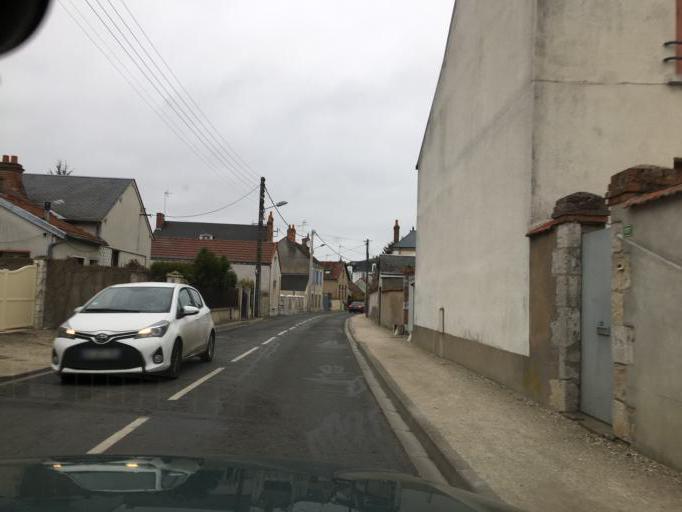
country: FR
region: Centre
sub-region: Departement du Loiret
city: Saint-Jean-le-Blanc
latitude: 47.8907
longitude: 1.9151
